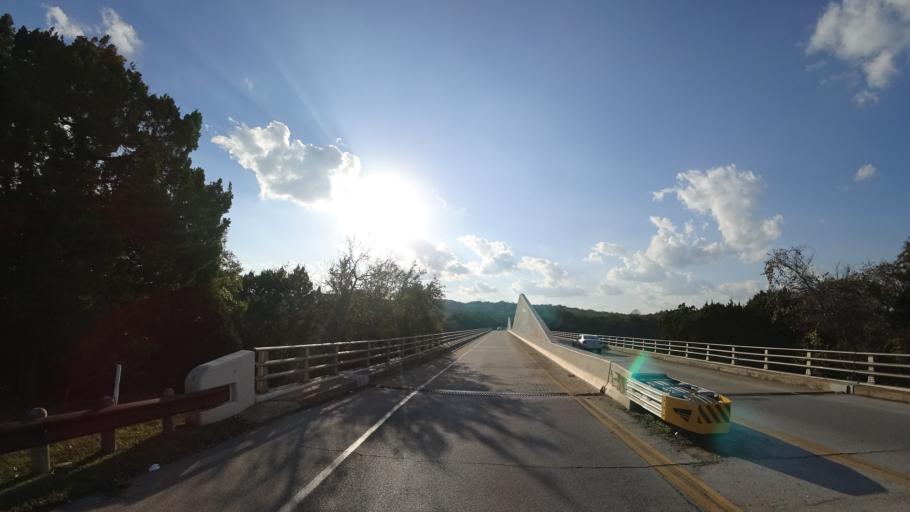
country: US
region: Texas
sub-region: Travis County
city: Lost Creek
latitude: 30.2965
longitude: -97.8505
